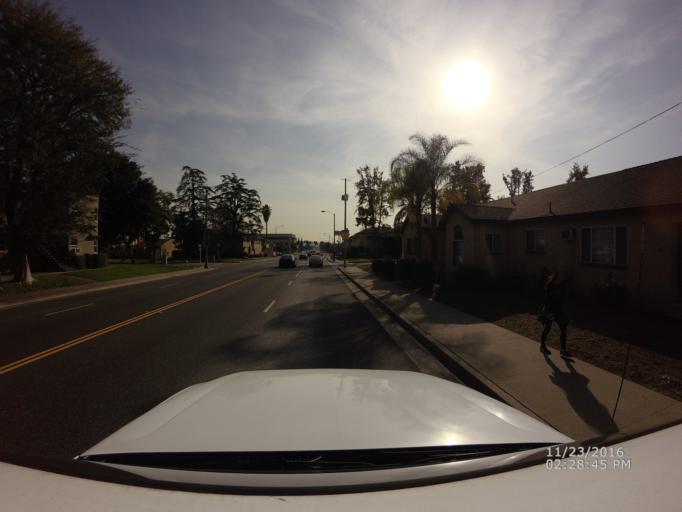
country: US
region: California
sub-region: Los Angeles County
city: South Pasadena
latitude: 34.0968
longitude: -118.1521
